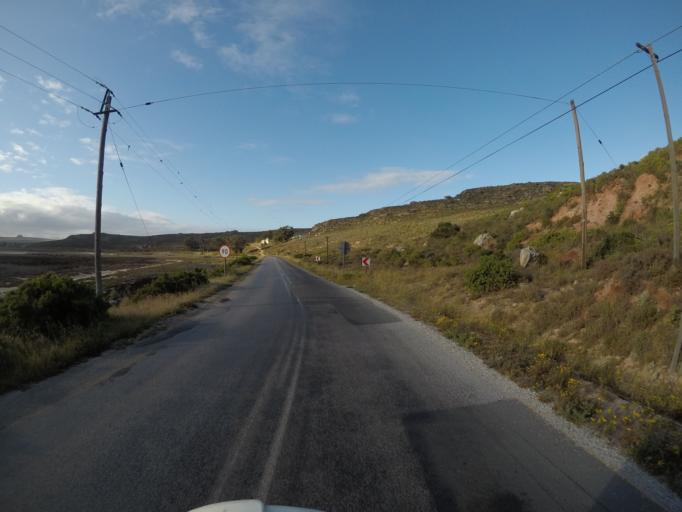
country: ZA
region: Western Cape
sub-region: West Coast District Municipality
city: Clanwilliam
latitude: -32.3188
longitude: 18.3576
